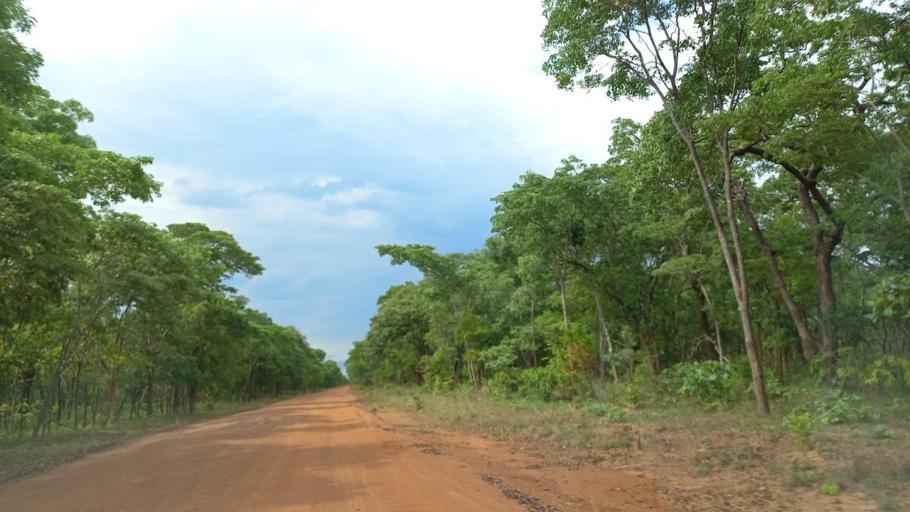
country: ZM
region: North-Western
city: Kalengwa
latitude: -13.3932
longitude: 25.0697
